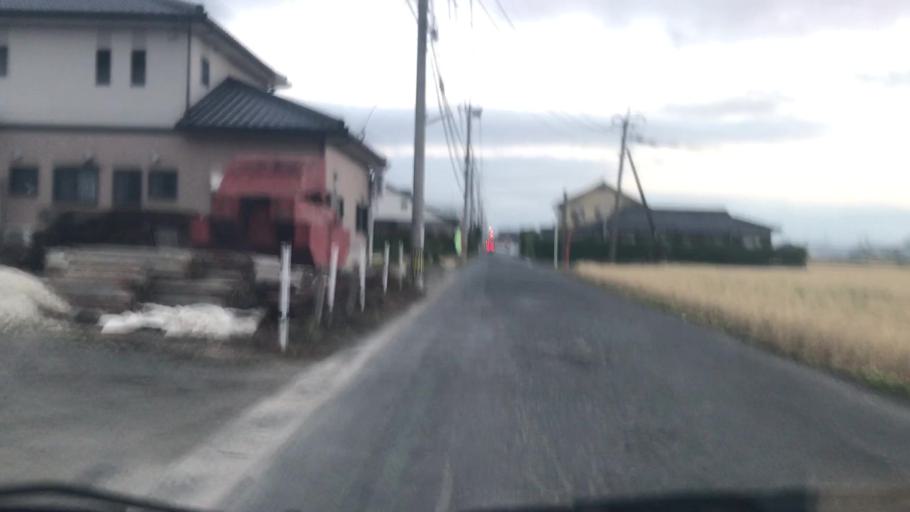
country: JP
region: Saga Prefecture
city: Saga-shi
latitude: 33.2305
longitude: 130.3019
